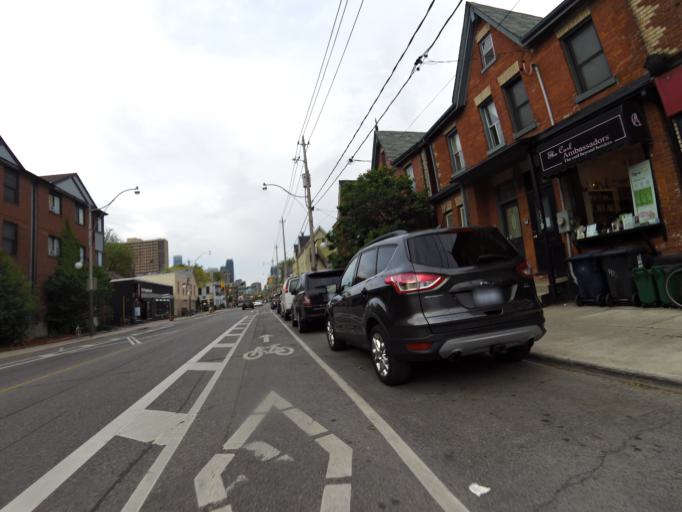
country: CA
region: Ontario
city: Toronto
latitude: 43.6620
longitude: -79.4071
